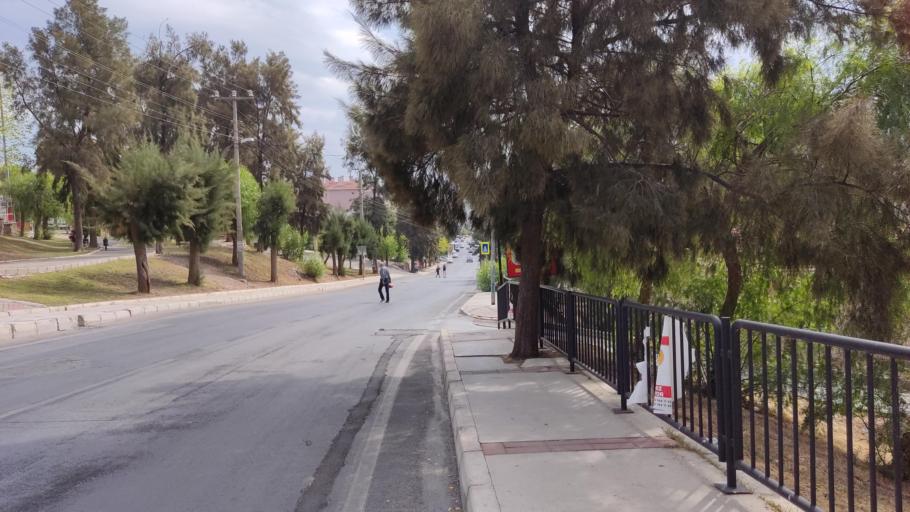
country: TR
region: Izmir
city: Karsiyaka
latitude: 38.4995
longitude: 27.0875
